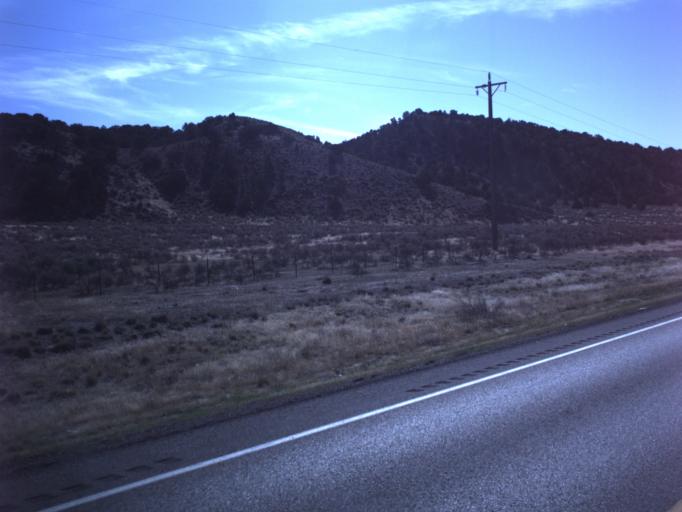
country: US
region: Utah
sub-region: Sanpete County
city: Gunnison
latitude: 39.3606
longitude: -111.9298
